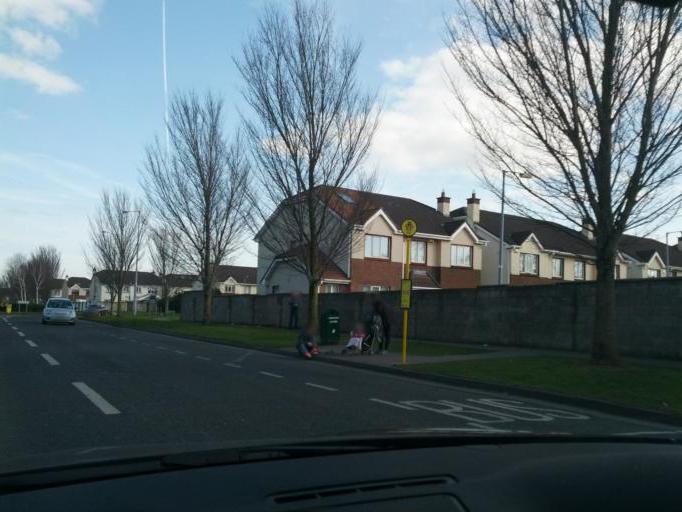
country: IE
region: Leinster
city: Lucan
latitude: 53.3399
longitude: -6.4265
